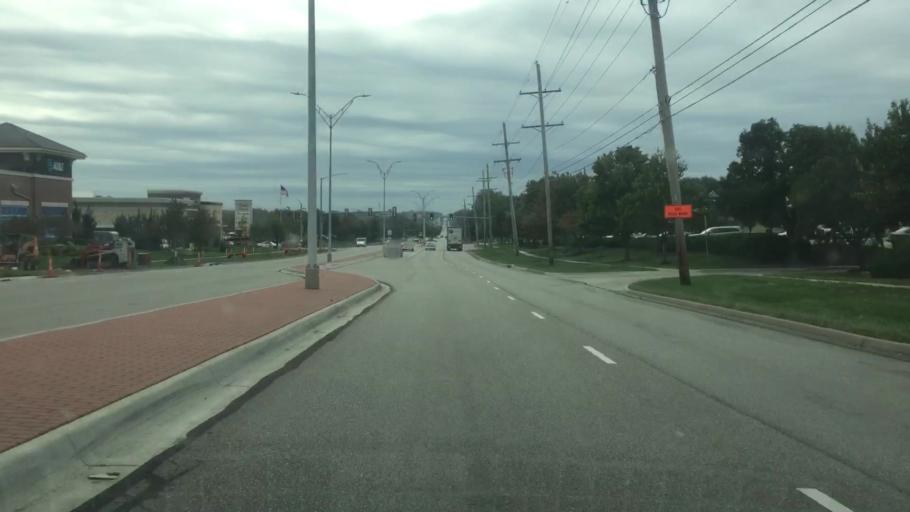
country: US
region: Kansas
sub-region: Johnson County
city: Lenexa
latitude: 38.9119
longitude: -94.7611
